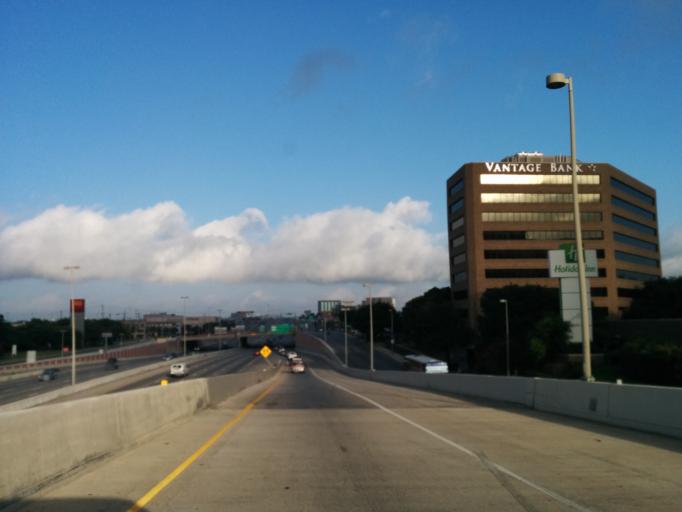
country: US
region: Texas
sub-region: Bexar County
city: Castle Hills
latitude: 29.5206
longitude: -98.4884
